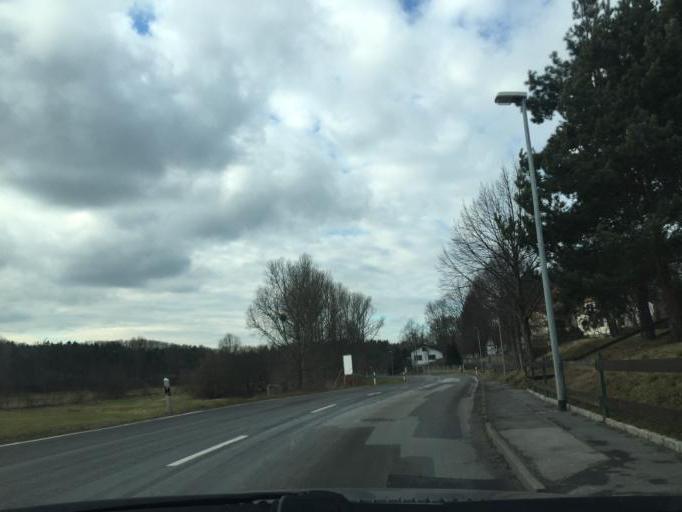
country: DE
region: Saxony
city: Ottendorf-Okrilla
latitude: 51.1801
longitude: 13.8072
